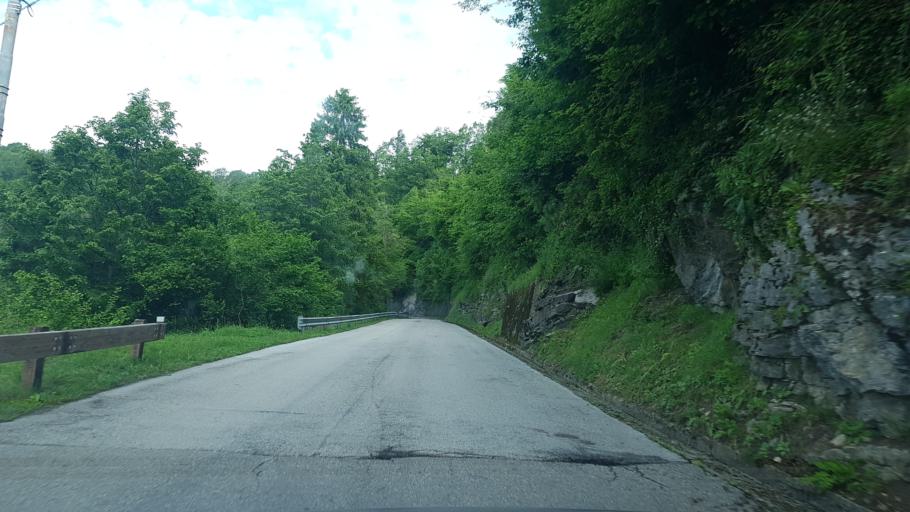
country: IT
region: Friuli Venezia Giulia
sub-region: Provincia di Udine
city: Arta Terme
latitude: 46.4677
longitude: 13.0153
